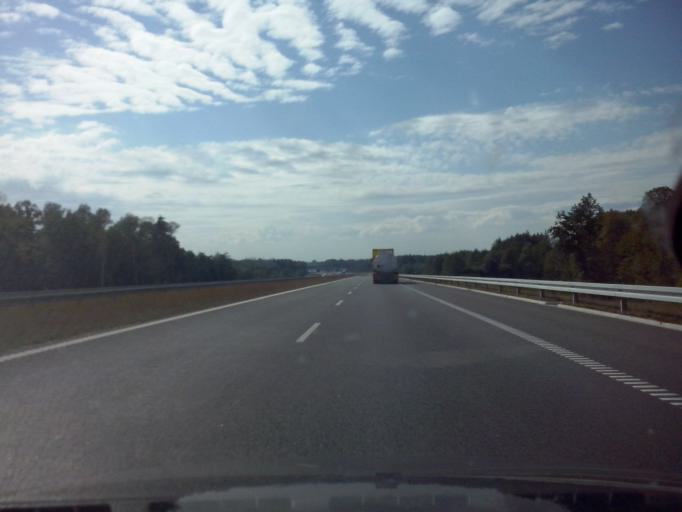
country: PL
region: Lesser Poland Voivodeship
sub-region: Powiat tarnowski
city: Jodlowka-Walki
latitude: 50.0966
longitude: 21.1828
